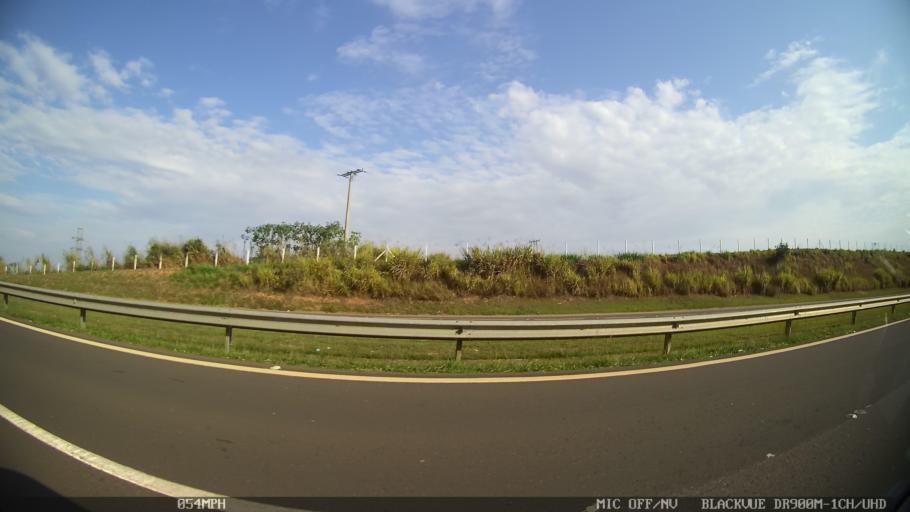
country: BR
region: Sao Paulo
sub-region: Cosmopolis
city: Cosmopolis
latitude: -22.6506
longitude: -47.2017
